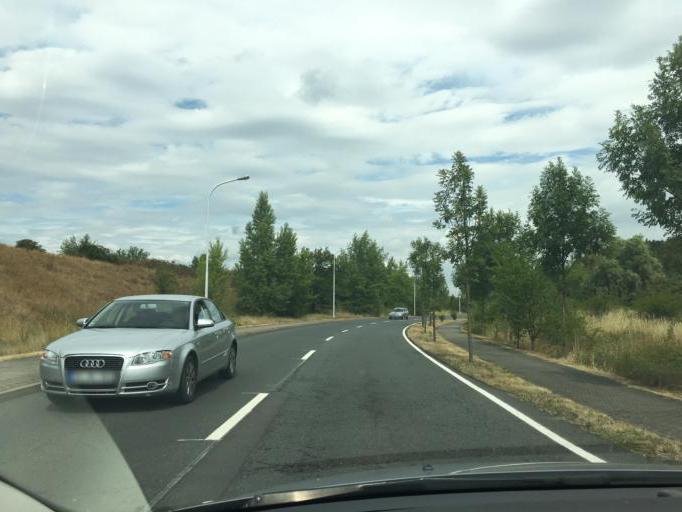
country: DE
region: Saxony-Anhalt
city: Angersdorf
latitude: 51.4389
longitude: 11.9479
